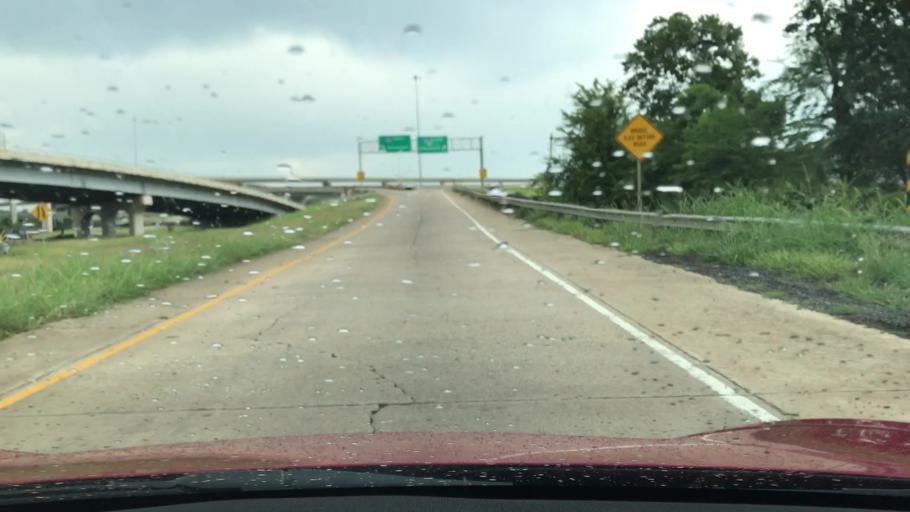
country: US
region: Louisiana
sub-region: Bossier Parish
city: Bossier City
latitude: 32.4194
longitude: -93.7549
